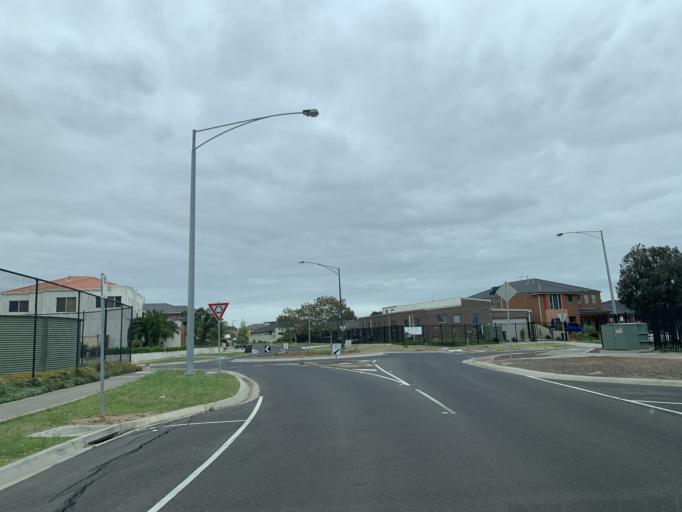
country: AU
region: Victoria
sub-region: Brimbank
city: Cairnlea
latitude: -37.7556
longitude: 144.7943
